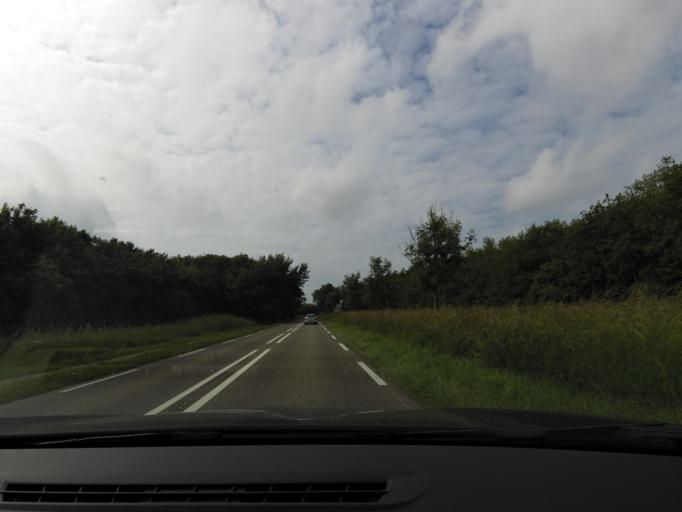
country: NL
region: Zeeland
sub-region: Gemeente Vlissingen
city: Vlissingen
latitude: 51.5237
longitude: 3.4509
